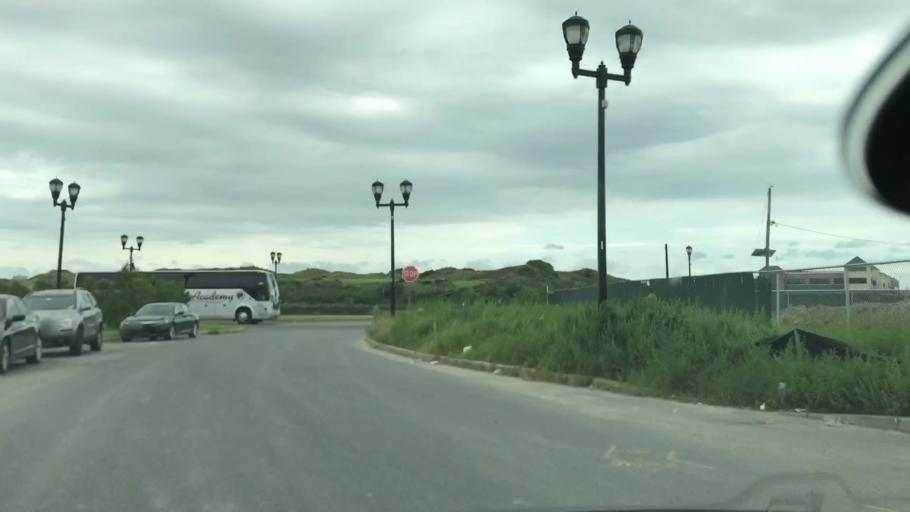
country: US
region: New Jersey
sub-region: Hudson County
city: Bayonne
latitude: 40.6703
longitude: -74.1000
